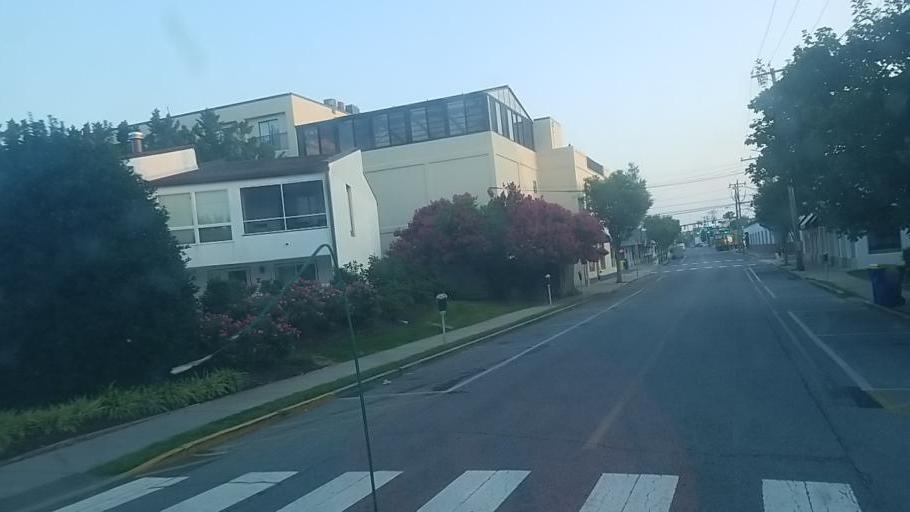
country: US
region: Delaware
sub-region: Sussex County
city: Rehoboth Beach
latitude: 38.7148
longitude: -75.0787
